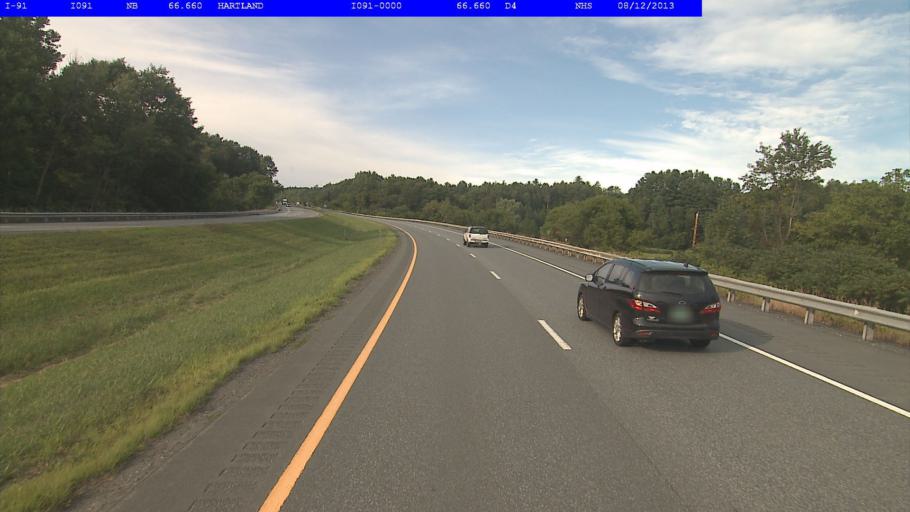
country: US
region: Vermont
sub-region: Windsor County
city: White River Junction
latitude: 43.5967
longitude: -72.3453
